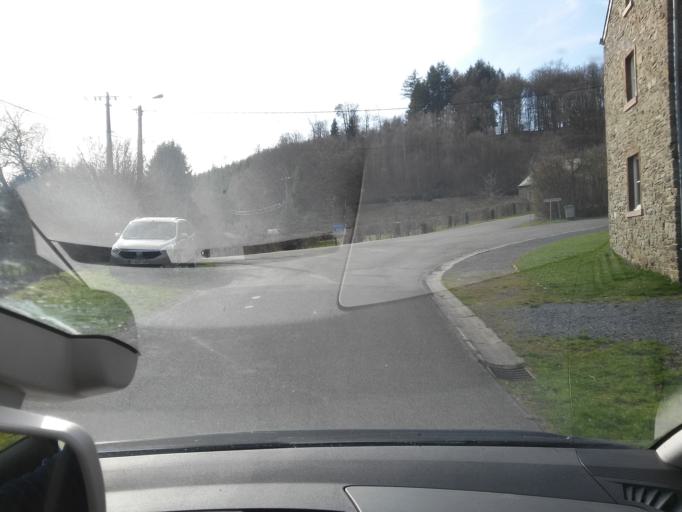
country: BE
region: Wallonia
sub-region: Province du Luxembourg
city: Daverdisse
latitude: 49.9933
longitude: 5.1532
